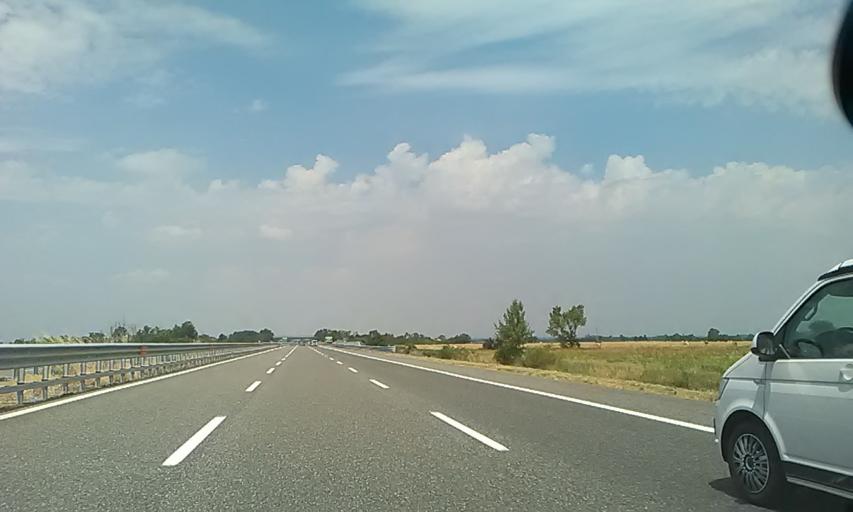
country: IT
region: Piedmont
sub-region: Provincia di Alessandria
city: Castelspina
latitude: 44.7987
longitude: 8.6077
